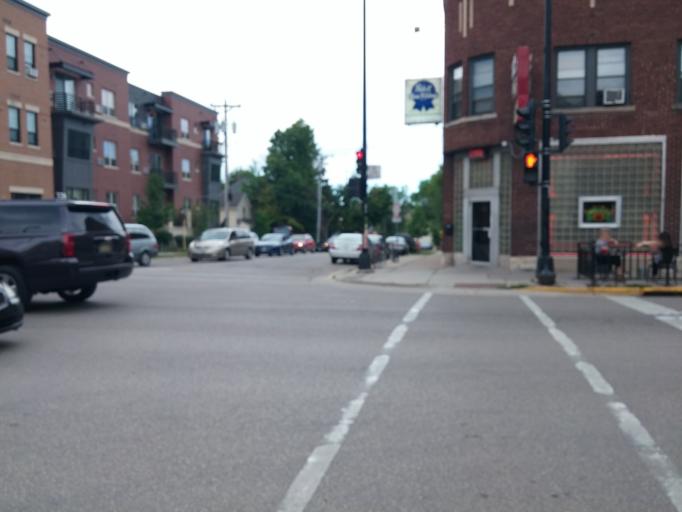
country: US
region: Wisconsin
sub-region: Dane County
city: Monona
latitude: 43.0844
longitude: -89.3624
